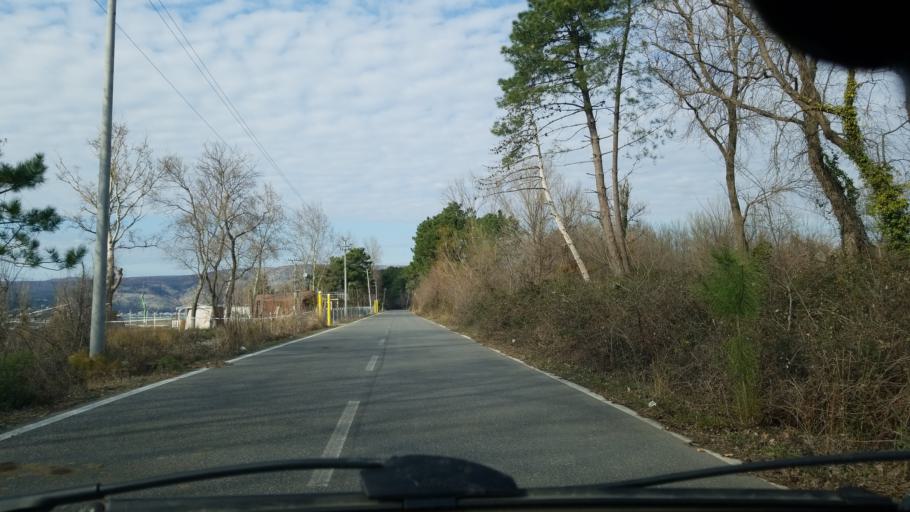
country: AL
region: Lezhe
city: Shengjin
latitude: 41.7770
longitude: 19.6033
